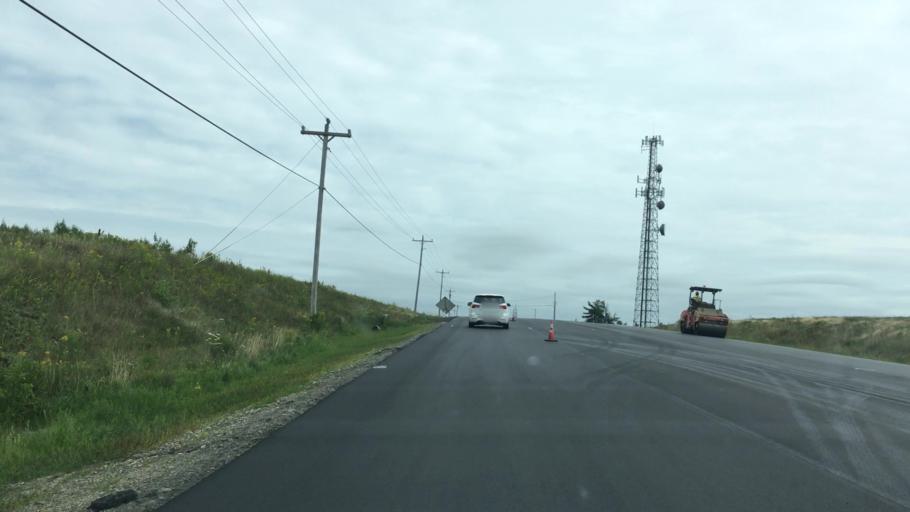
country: US
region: Maine
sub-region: Washington County
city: Machias
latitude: 44.9639
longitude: -67.6513
